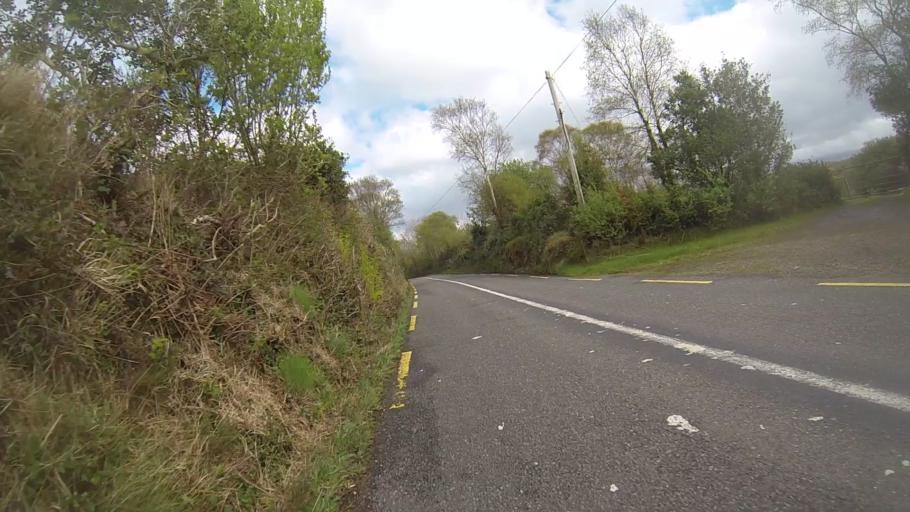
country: IE
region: Munster
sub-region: Ciarrai
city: Kenmare
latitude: 51.8266
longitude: -9.8484
